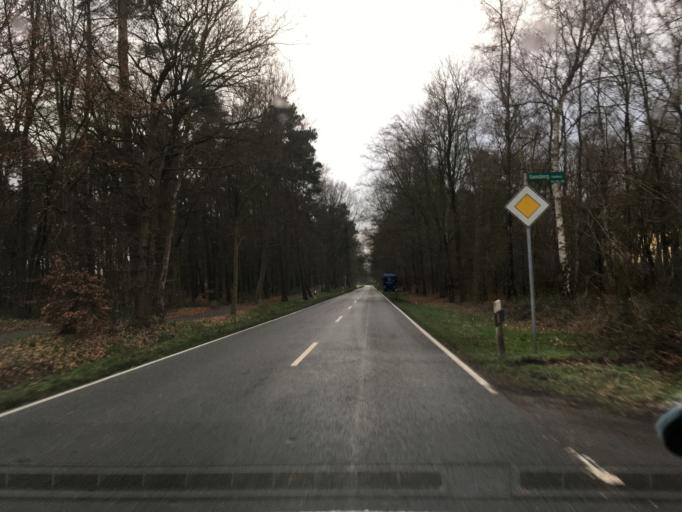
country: DE
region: North Rhine-Westphalia
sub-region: Regierungsbezirk Munster
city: Schoppingen
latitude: 52.0944
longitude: 7.2127
